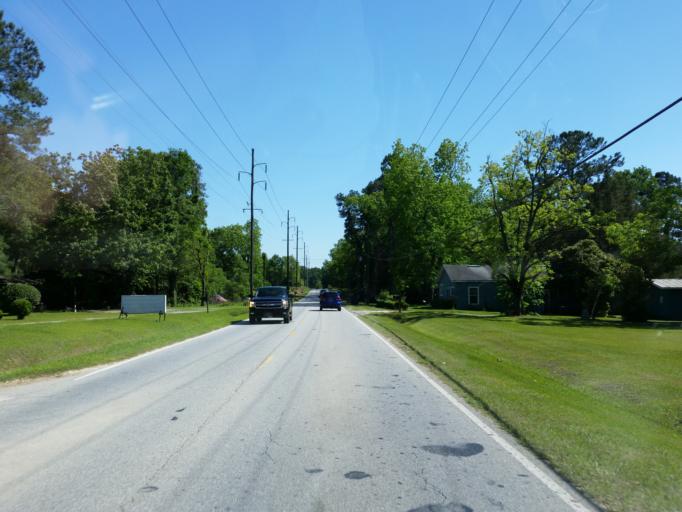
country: US
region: Georgia
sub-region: Lowndes County
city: Hahira
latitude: 30.9294
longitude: -83.3499
